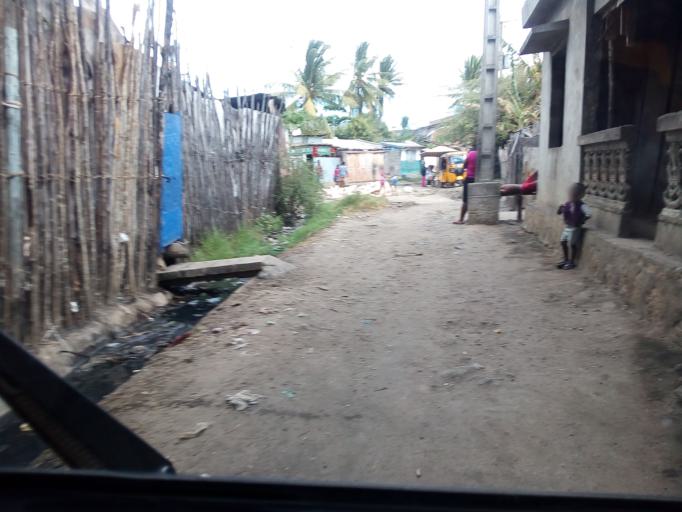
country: MG
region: Boeny
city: Mahajanga
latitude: -15.7175
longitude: 46.3280
